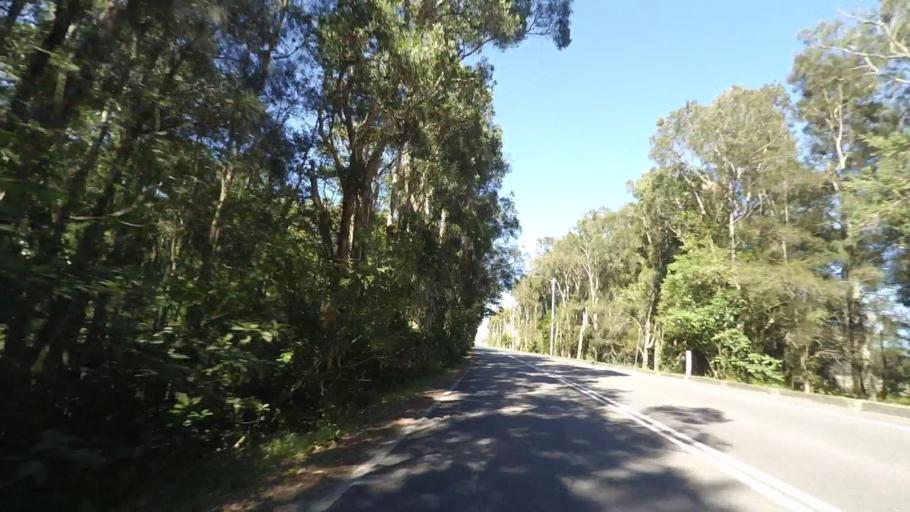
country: AU
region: New South Wales
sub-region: Great Lakes
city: Hawks Nest
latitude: -32.6671
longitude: 152.1733
